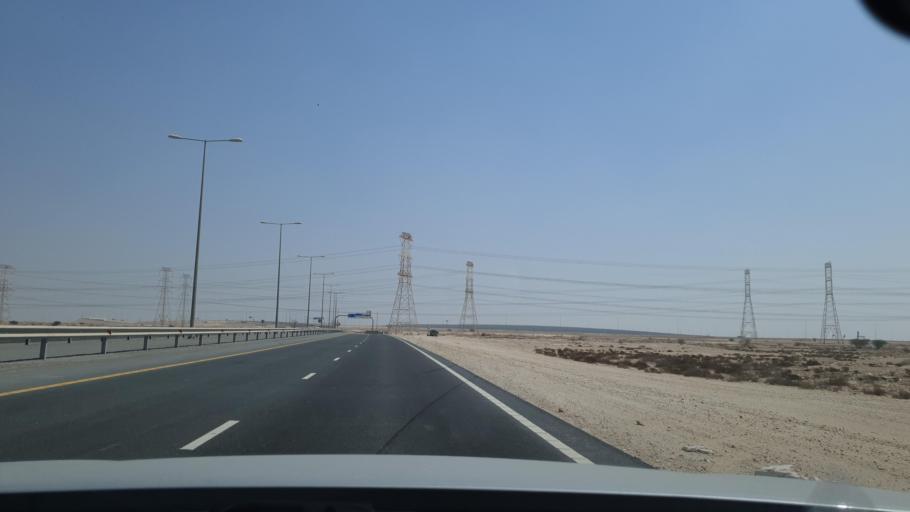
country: QA
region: Baladiyat az Za`ayin
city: Az Za`ayin
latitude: 25.6198
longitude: 51.3513
